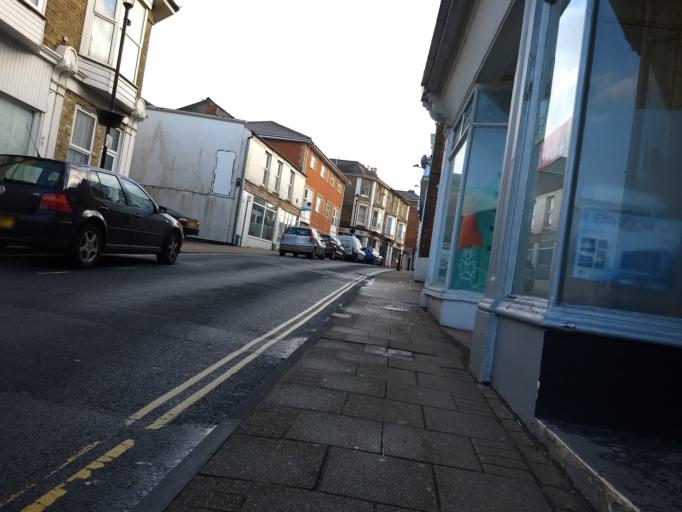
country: GB
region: England
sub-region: Isle of Wight
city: Ryde
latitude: 50.7254
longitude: -1.1636
